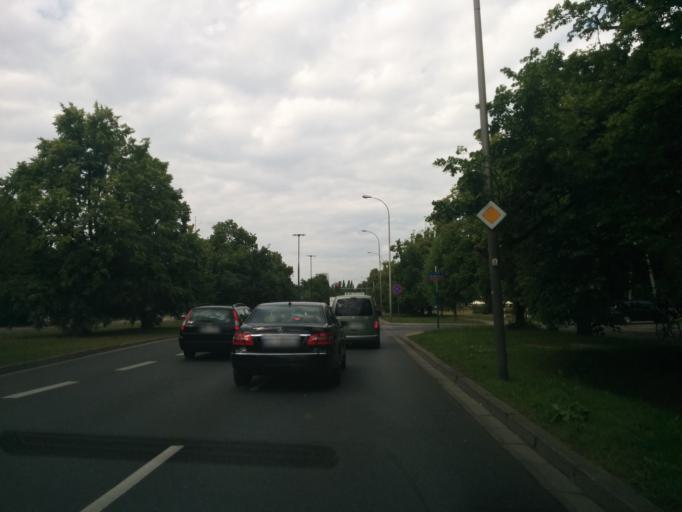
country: PL
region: Masovian Voivodeship
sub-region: Warszawa
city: Ochota
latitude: 52.2089
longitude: 20.9877
